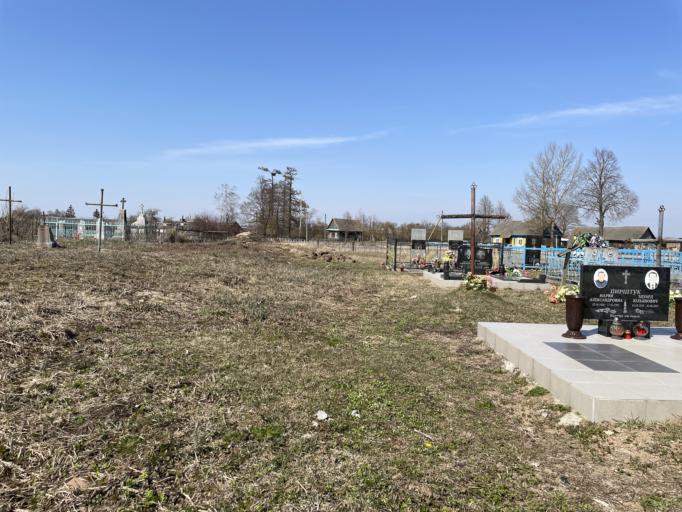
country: BY
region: Minsk
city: Snow
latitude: 53.1467
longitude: 26.3598
